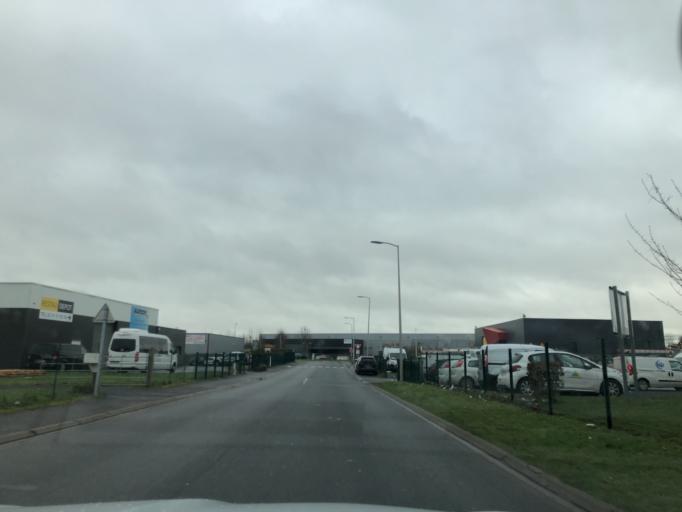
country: FR
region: Lower Normandy
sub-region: Departement du Calvados
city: Giberville
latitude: 49.1703
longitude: -0.2942
